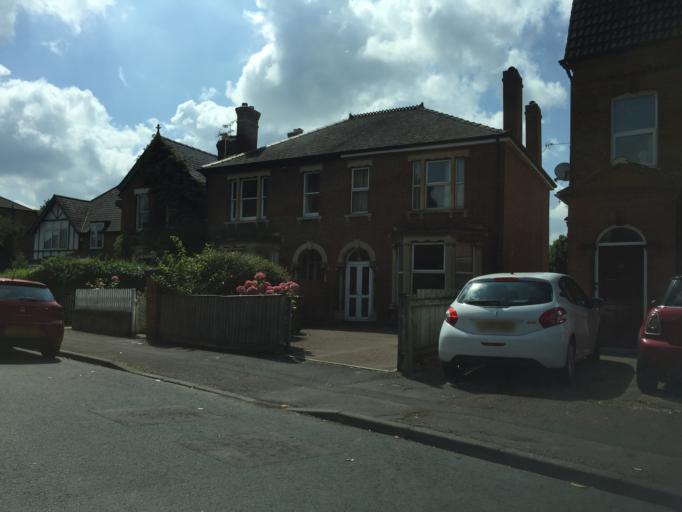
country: GB
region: England
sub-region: Gloucestershire
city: Gloucester
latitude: 51.8719
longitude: -2.2358
